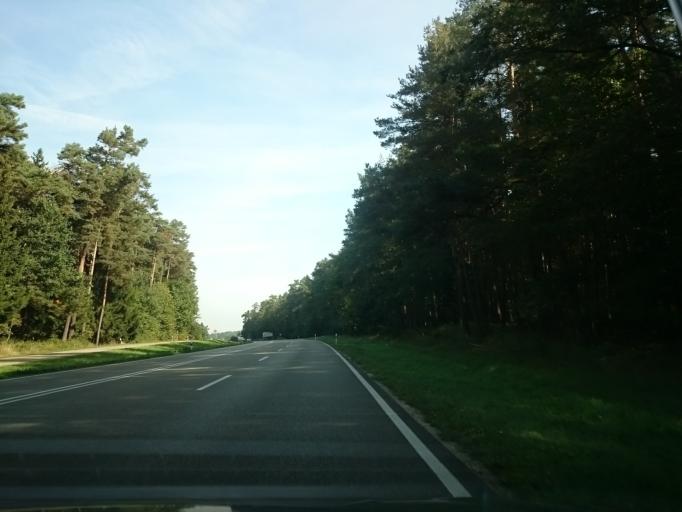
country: DE
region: Bavaria
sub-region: Upper Bavaria
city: Gachenbach
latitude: 48.5073
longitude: 11.2178
